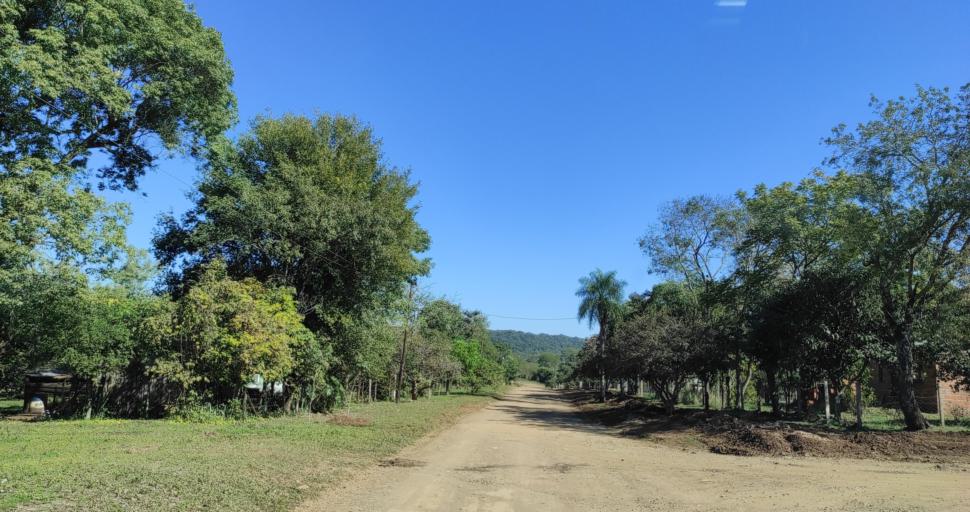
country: AR
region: Misiones
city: Cerro Cora
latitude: -27.5631
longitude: -55.7036
